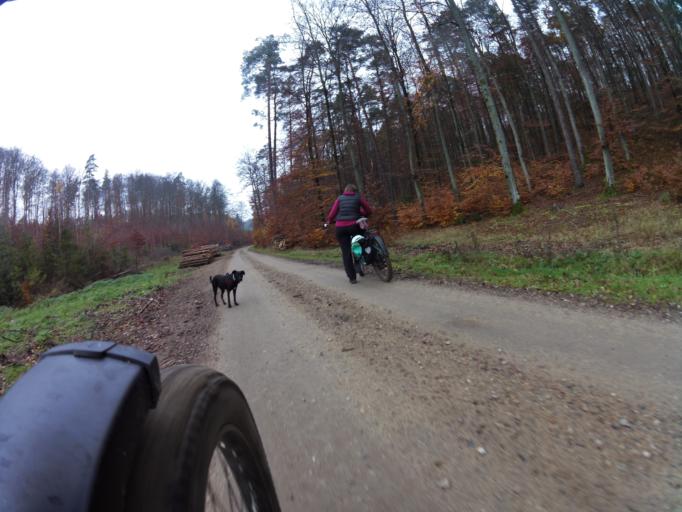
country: PL
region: Pomeranian Voivodeship
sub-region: Powiat wejherowski
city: Orle
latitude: 54.7037
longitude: 18.1455
